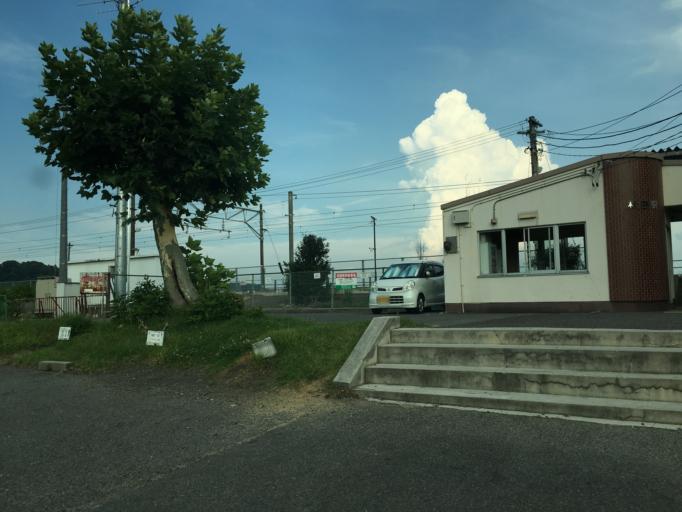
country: JP
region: Fukushima
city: Nihommatsu
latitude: 37.5633
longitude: 140.4135
